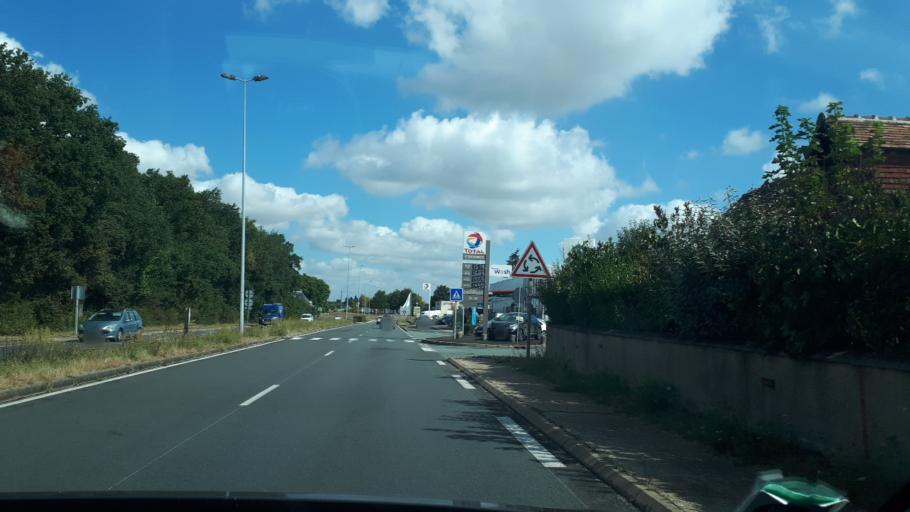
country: FR
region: Centre
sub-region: Departement du Loir-et-Cher
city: Saint-Ouen
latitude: 47.8157
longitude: 1.0758
